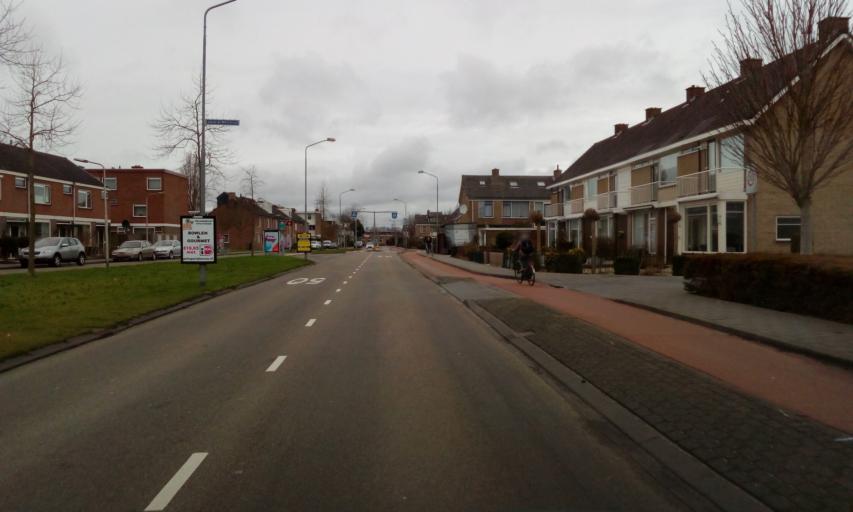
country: NL
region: South Holland
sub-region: Gemeente Alblasserdam
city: Alblasserdam
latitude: 51.8690
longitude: 4.6546
